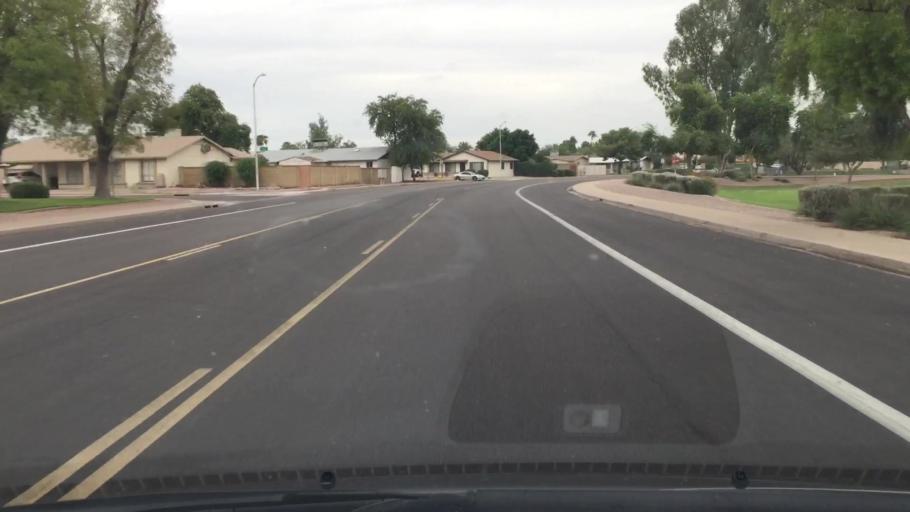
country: US
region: Arizona
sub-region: Maricopa County
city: Gilbert
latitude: 33.3960
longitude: -111.7618
